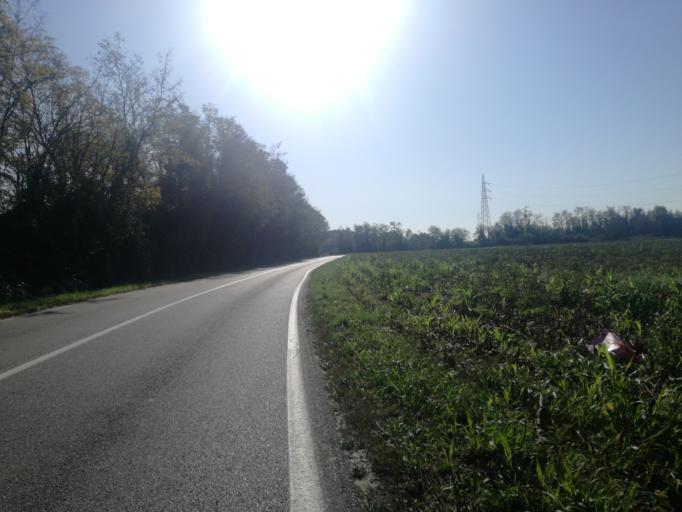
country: IT
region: Lombardy
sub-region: Provincia di Monza e Brianza
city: Cornate d'Adda
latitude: 45.6367
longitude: 9.4881
